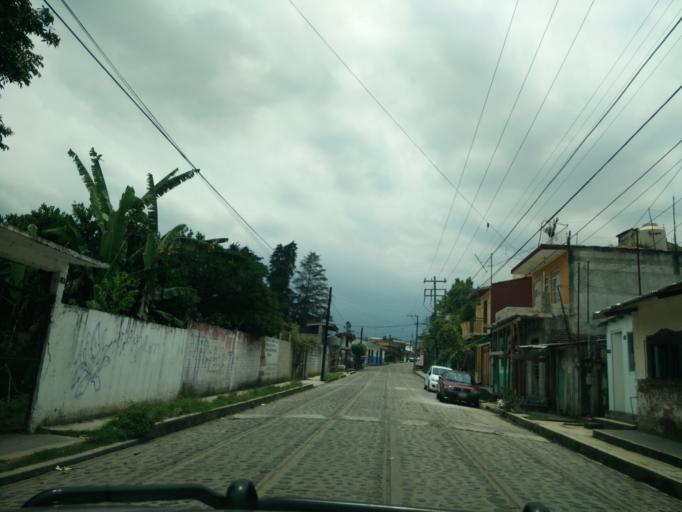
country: MX
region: Veracruz
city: Xico
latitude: 19.4171
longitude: -96.9999
